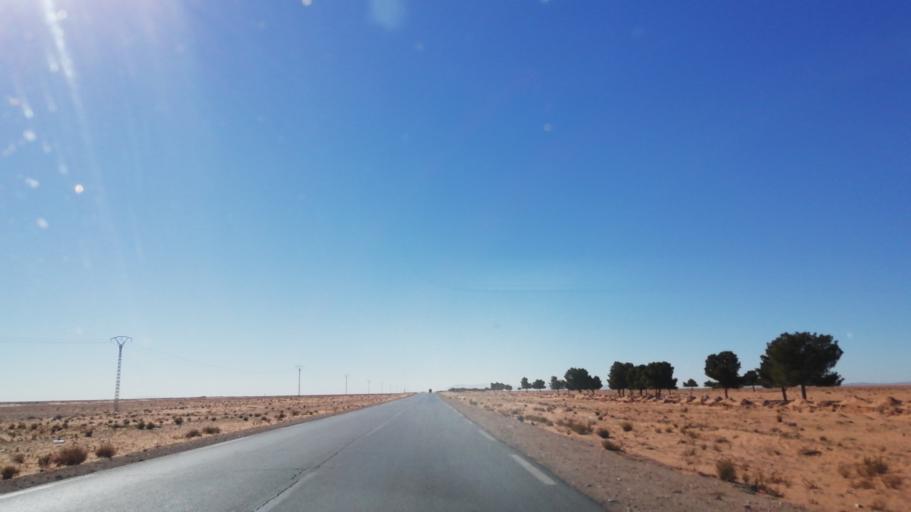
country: DZ
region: Wilaya de Naama
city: Naama
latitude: 33.9712
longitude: 0.0211
